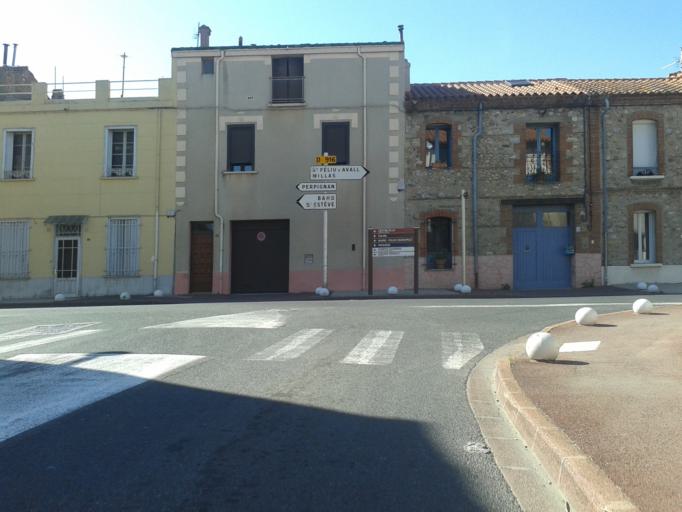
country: FR
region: Languedoc-Roussillon
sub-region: Departement des Pyrenees-Orientales
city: Le Soler
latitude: 42.6816
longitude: 2.7914
